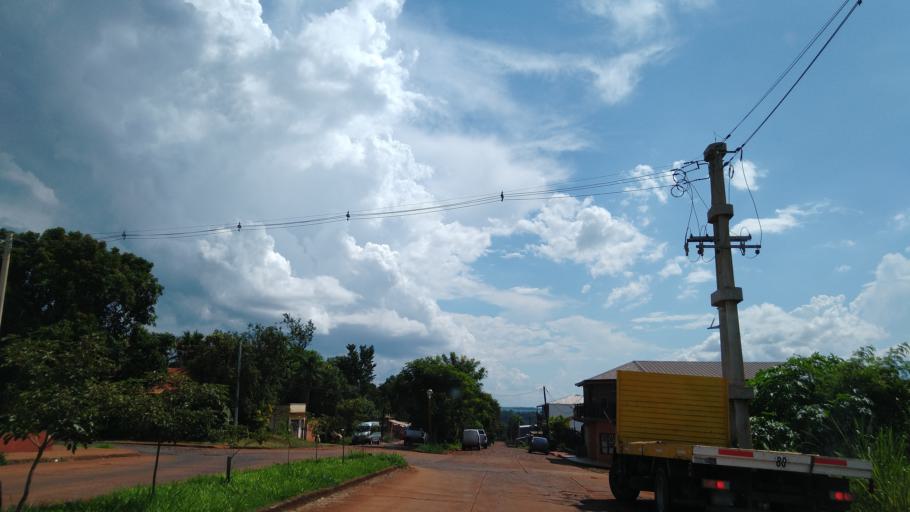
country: AR
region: Misiones
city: Puerto Libertad
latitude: -25.9678
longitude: -54.5712
